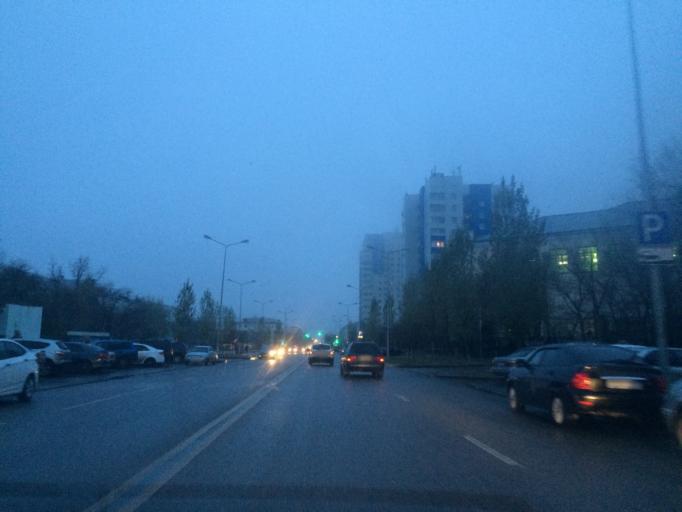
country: KZ
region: Astana Qalasy
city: Astana
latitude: 51.1857
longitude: 71.4120
